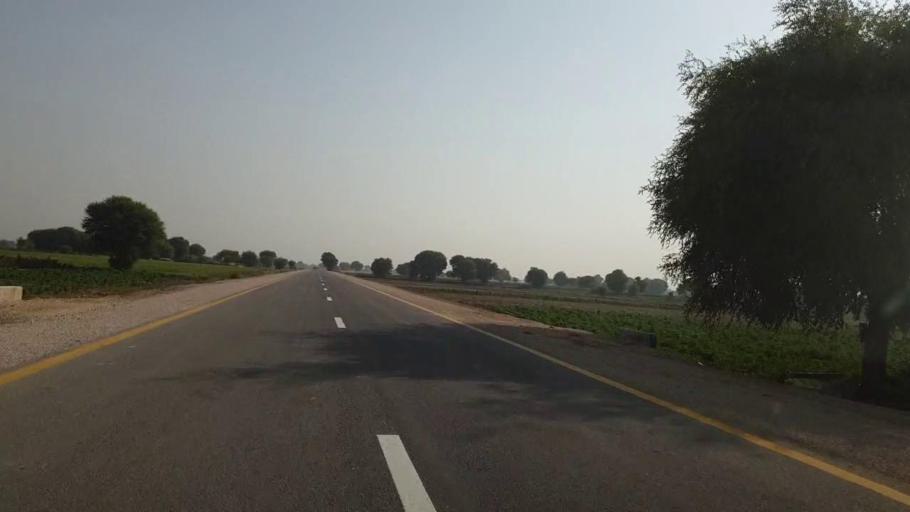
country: PK
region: Sindh
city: Bhan
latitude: 26.5304
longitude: 67.7889
